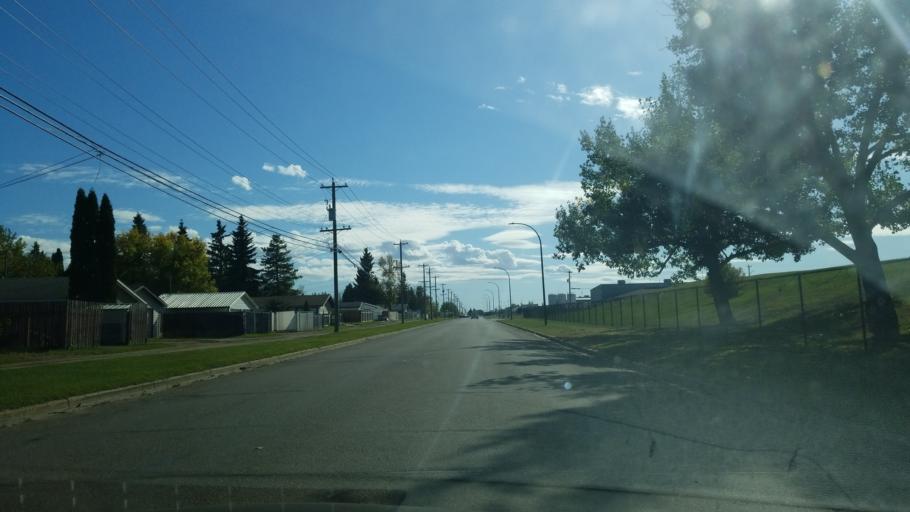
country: CA
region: Saskatchewan
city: Lloydminster
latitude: 53.2824
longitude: -110.0299
